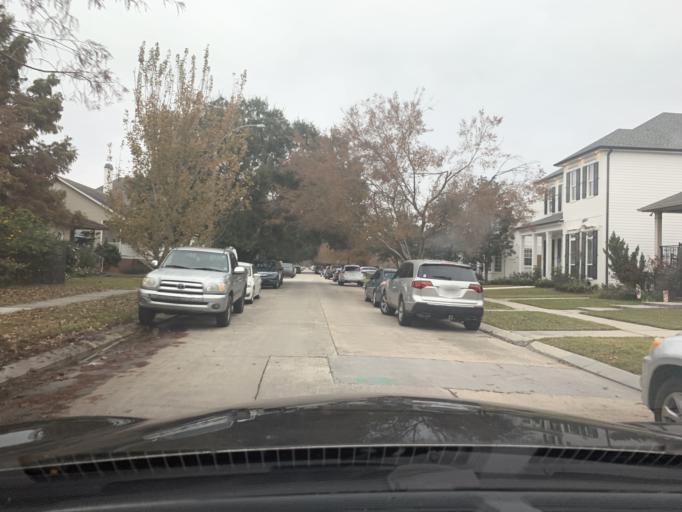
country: US
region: Louisiana
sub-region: Jefferson Parish
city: Metairie
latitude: 30.0095
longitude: -90.1062
